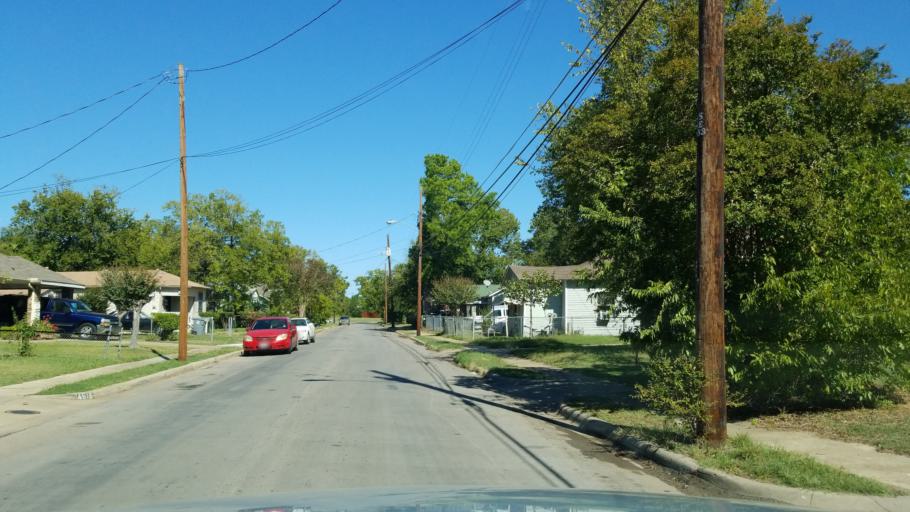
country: US
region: Texas
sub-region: Dallas County
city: Dallas
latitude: 32.7777
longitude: -96.7455
